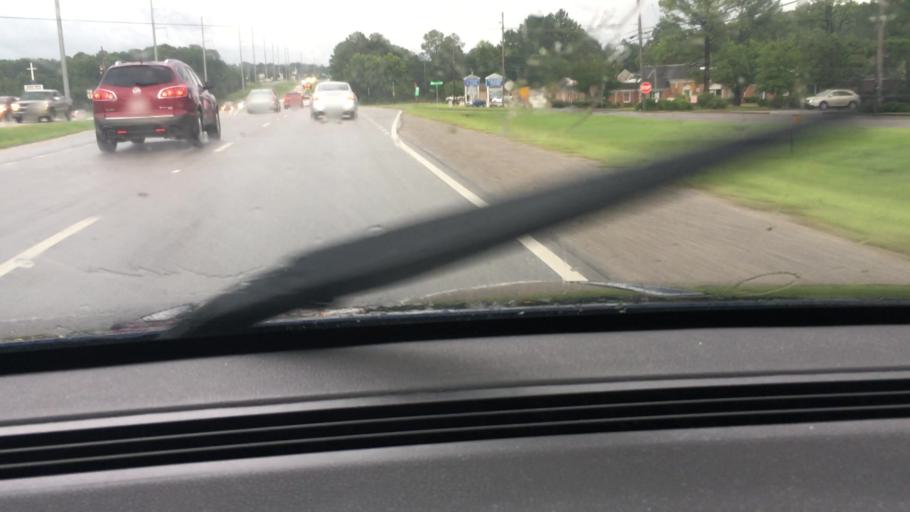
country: US
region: Alabama
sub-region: Tuscaloosa County
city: Northport
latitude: 33.2354
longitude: -87.5505
